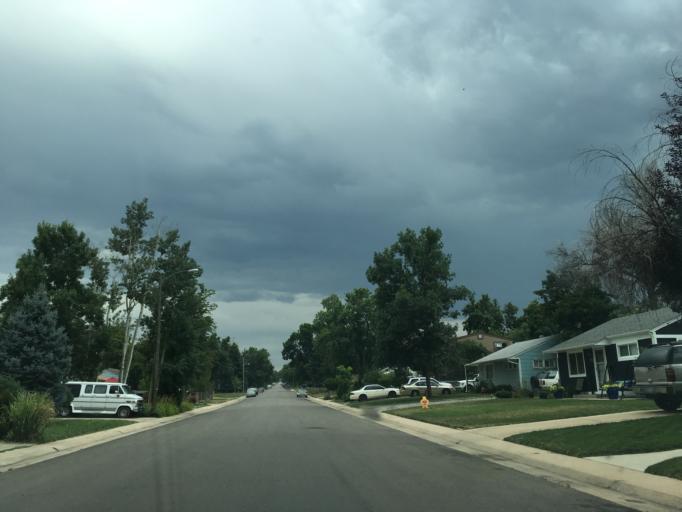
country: US
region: Colorado
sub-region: Arapahoe County
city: Sheridan
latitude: 39.6718
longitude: -105.0320
